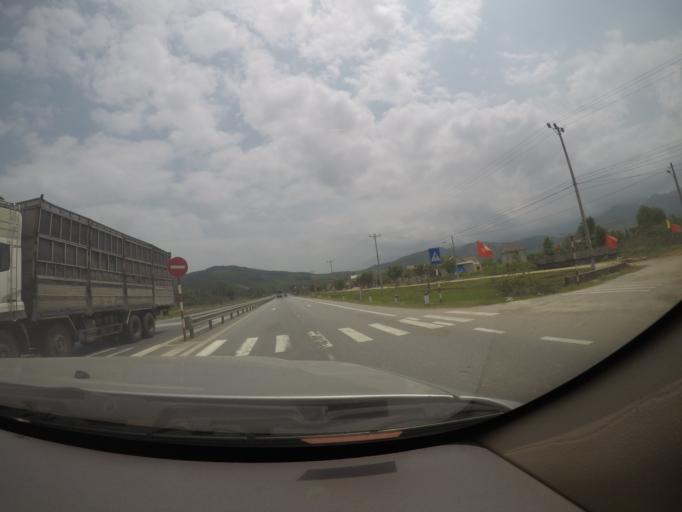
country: VN
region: Thua Thien-Hue
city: Phu Loc
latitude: 16.2688
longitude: 107.8905
